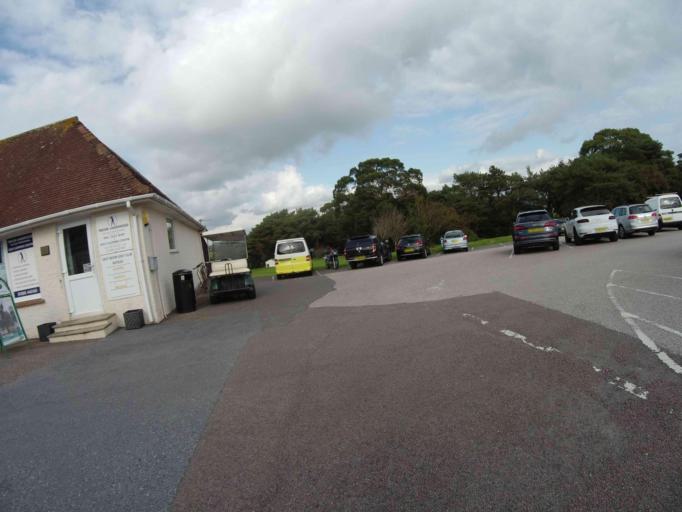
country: GB
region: England
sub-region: Devon
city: Budleigh Salterton
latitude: 50.6271
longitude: -3.3389
